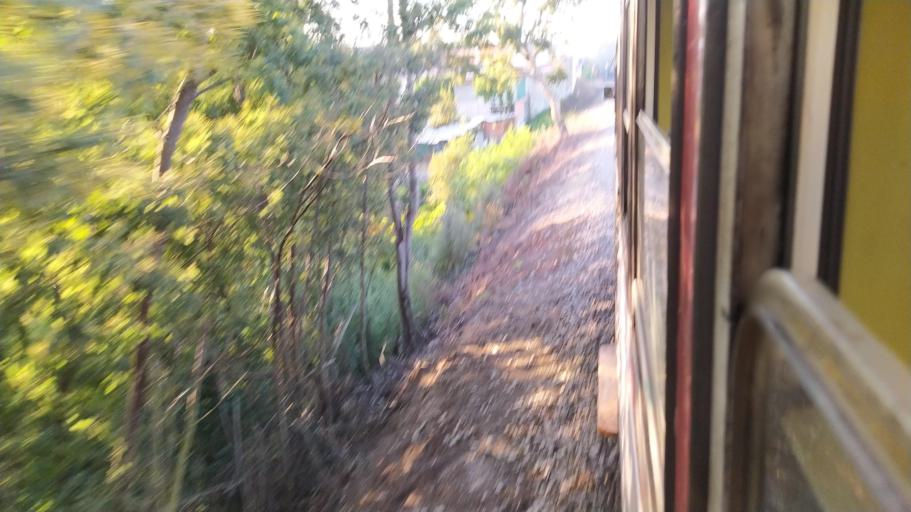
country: PT
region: Aveiro
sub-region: Aveiro
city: Eixo
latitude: 40.6321
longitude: -8.5709
